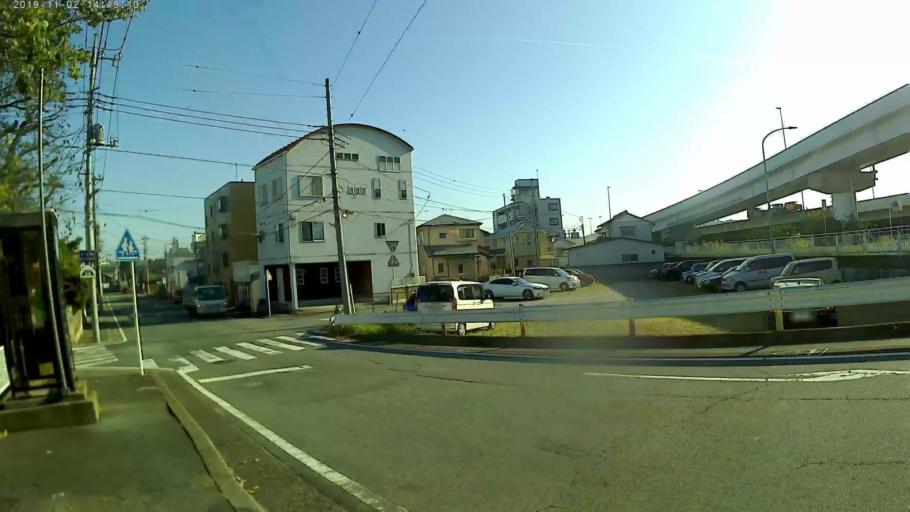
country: JP
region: Gunma
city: Takasaki
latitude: 36.3331
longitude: 138.9923
